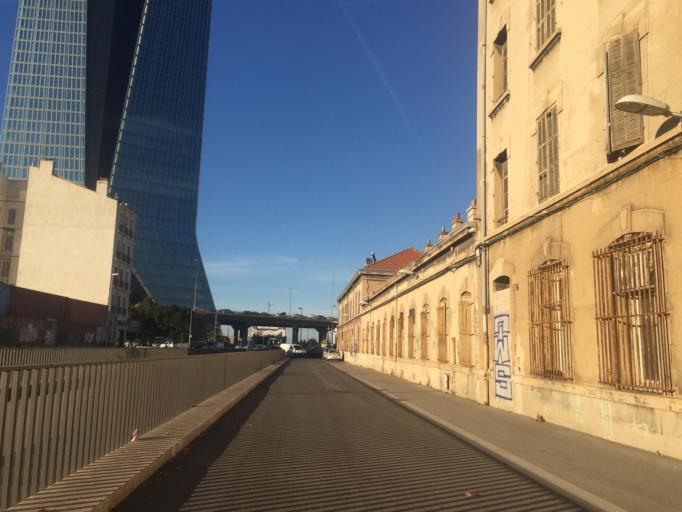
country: FR
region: Provence-Alpes-Cote d'Azur
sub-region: Departement des Bouches-du-Rhone
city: Marseille 03
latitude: 43.3164
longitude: 5.3679
